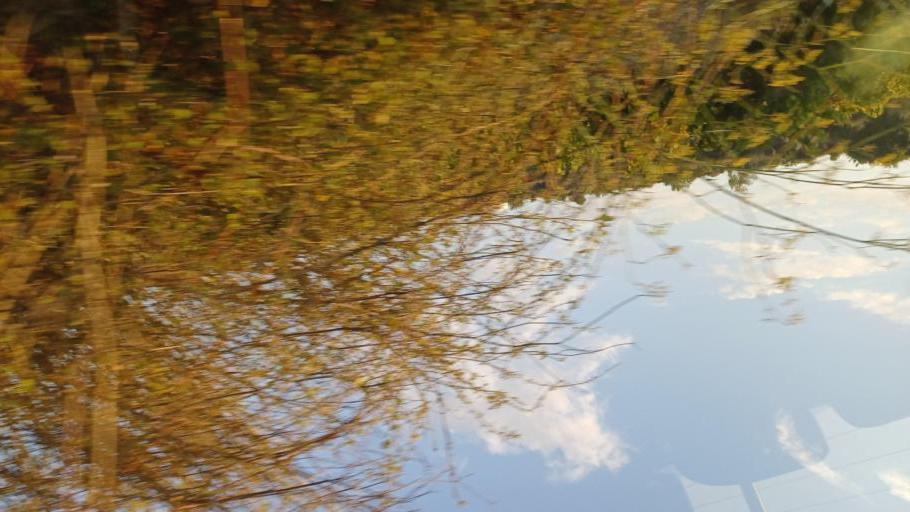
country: CY
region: Pafos
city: Tala
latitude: 34.8992
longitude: 32.4996
